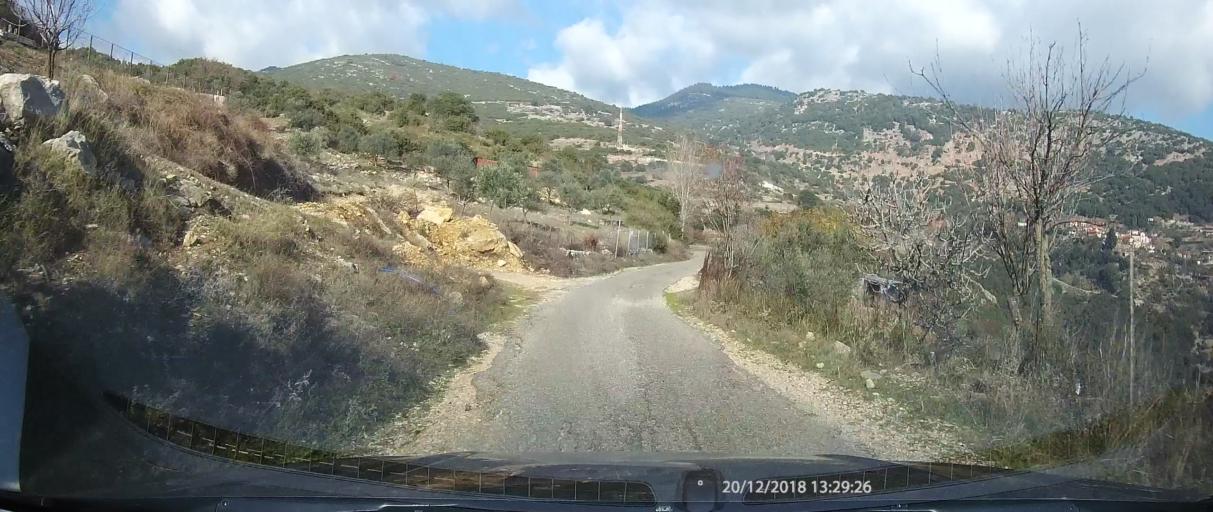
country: GR
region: West Greece
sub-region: Nomos Aitolias kai Akarnanias
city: Paravola
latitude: 38.6288
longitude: 21.5795
